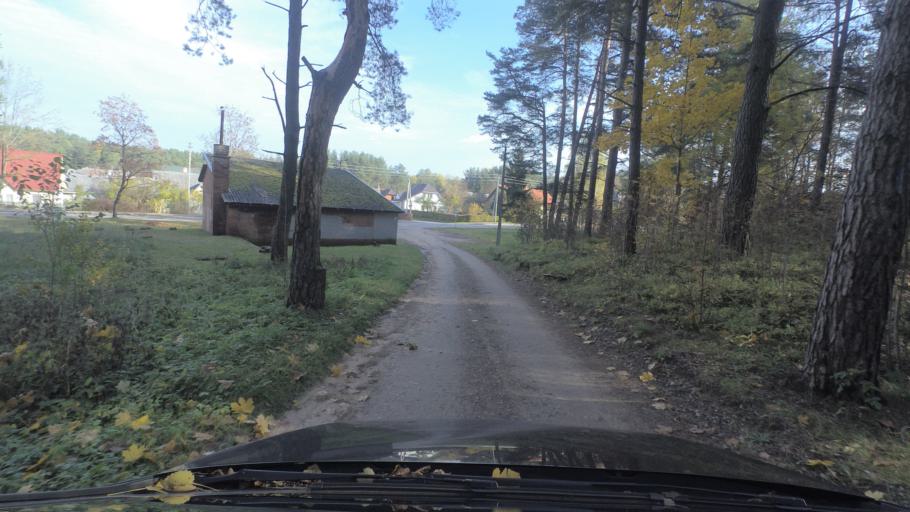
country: LT
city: Ignalina
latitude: 55.3410
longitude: 26.1756
